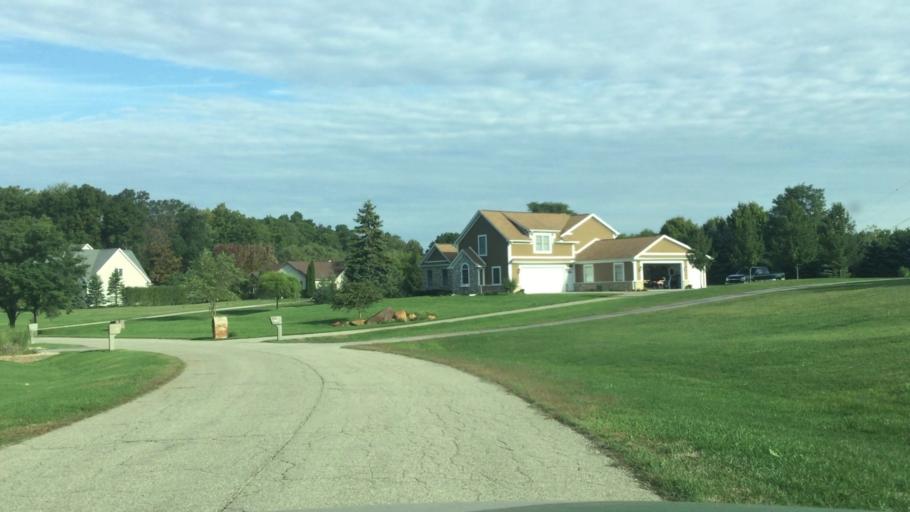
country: US
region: Michigan
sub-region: Livingston County
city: Howell
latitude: 42.6051
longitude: -83.8659
